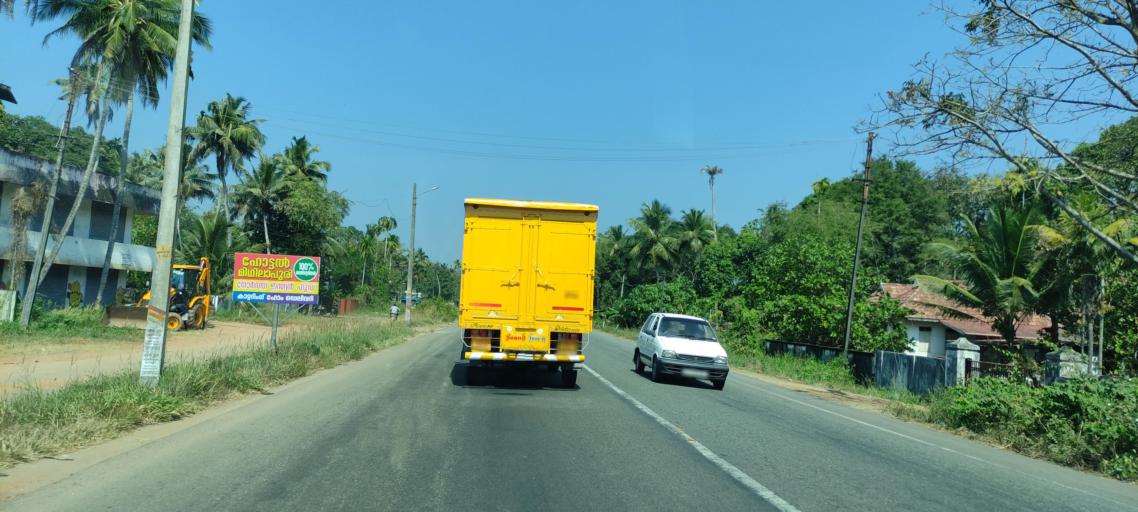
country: IN
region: Kerala
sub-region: Alappuzha
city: Kayankulam
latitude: 9.2305
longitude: 76.4740
